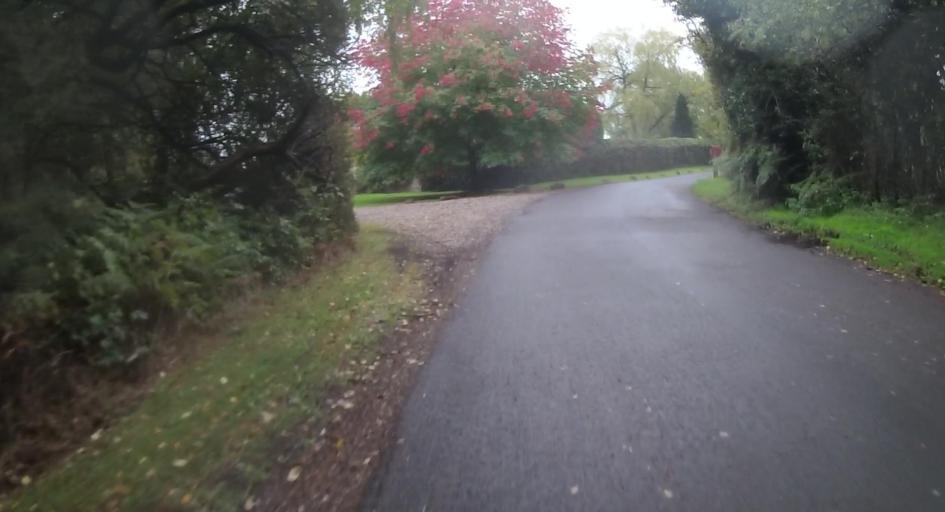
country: GB
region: England
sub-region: West Berkshire
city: Thatcham
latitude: 51.4141
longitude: -1.2138
